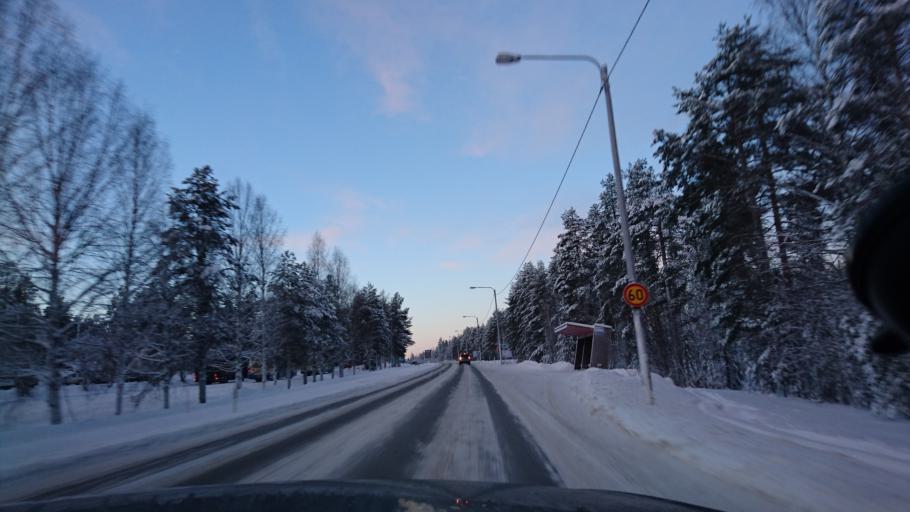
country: FI
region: Lapland
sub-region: Rovaniemi
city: Ranua
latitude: 65.9432
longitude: 26.4716
